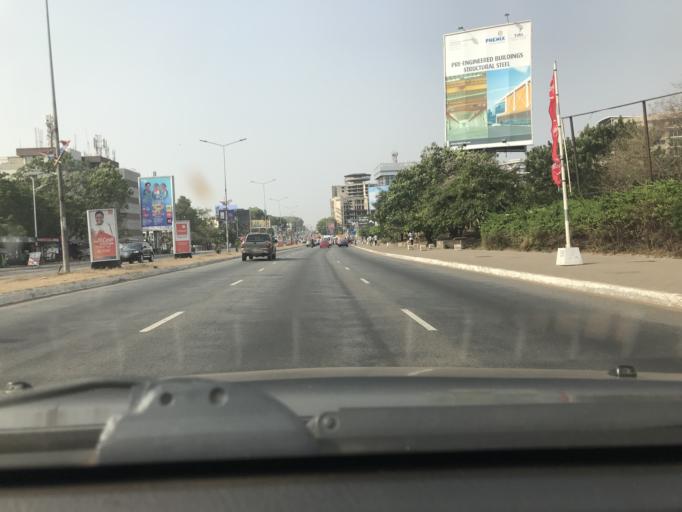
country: GH
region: Greater Accra
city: Accra
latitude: 5.5975
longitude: -0.1793
